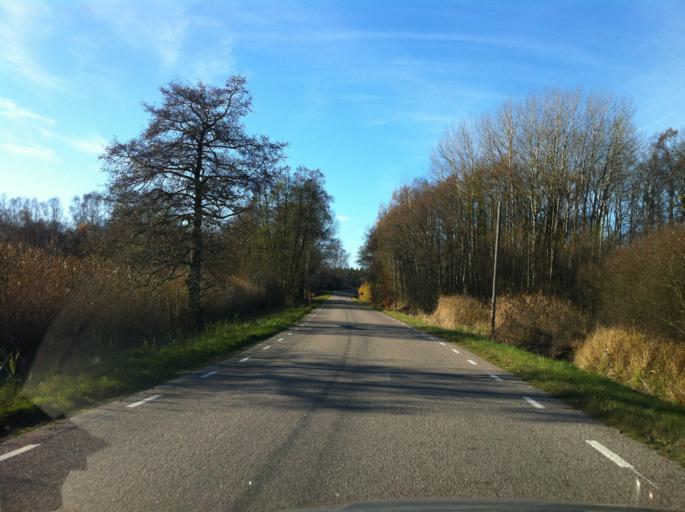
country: SE
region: Blekinge
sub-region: Ronneby Kommun
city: Brakne-Hoby
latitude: 56.1719
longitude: 15.1445
